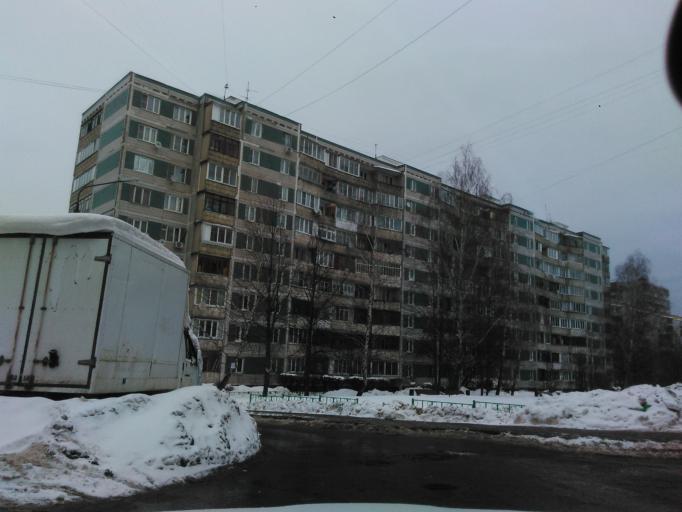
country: RU
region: Moskovskaya
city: Andreyevka
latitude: 55.9763
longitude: 37.1402
